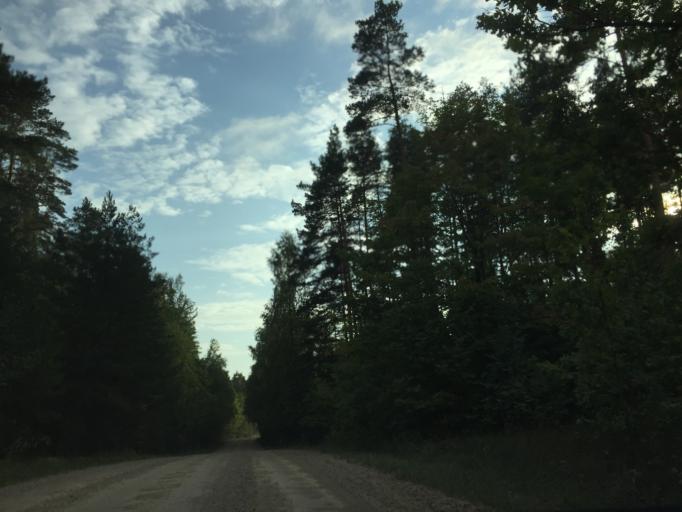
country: LV
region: Ikskile
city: Ikskile
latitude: 56.8100
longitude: 24.4467
